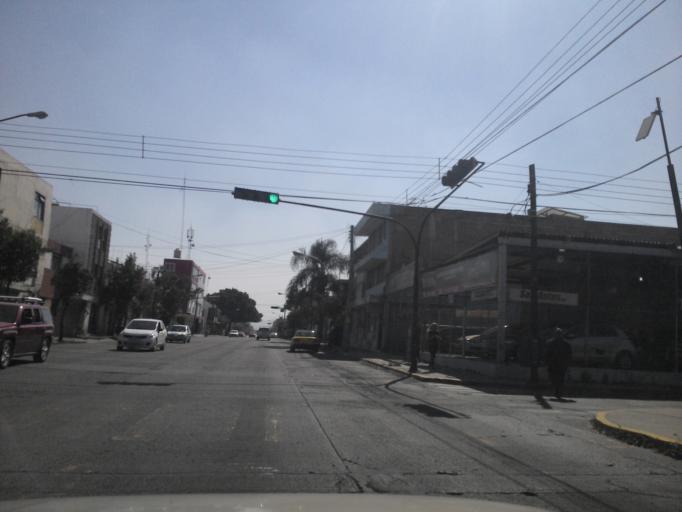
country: MX
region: Jalisco
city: Guadalajara
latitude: 20.6849
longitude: -103.3592
